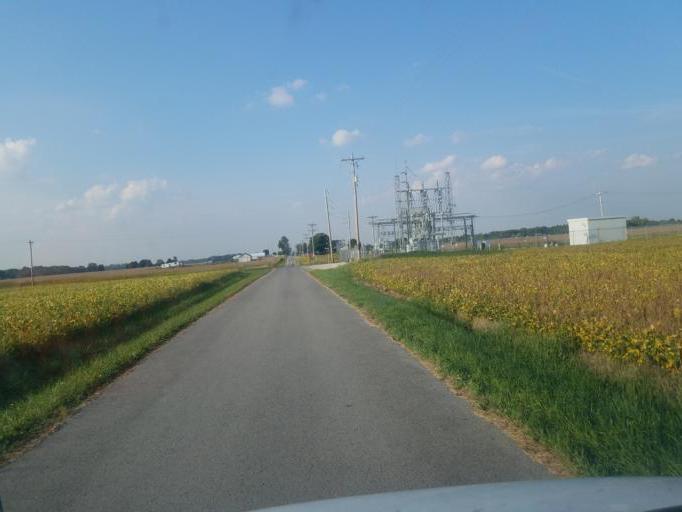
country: US
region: Ohio
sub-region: Seneca County
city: Tiffin
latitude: 40.9635
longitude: -83.1126
